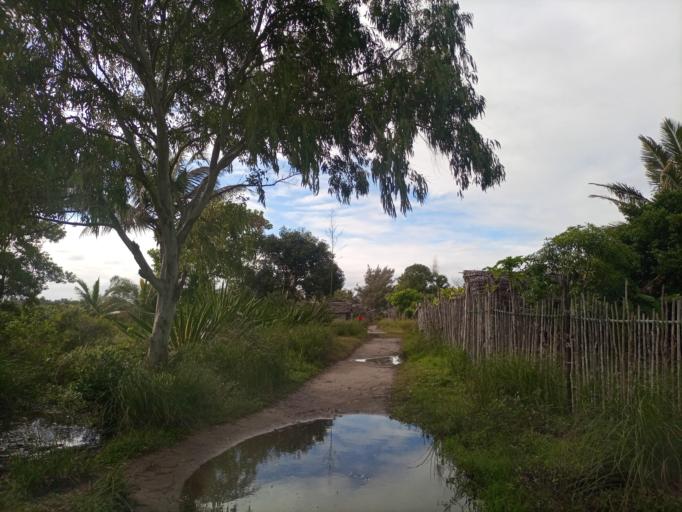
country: MG
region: Anosy
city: Fort Dauphin
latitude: -24.7796
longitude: 47.1897
